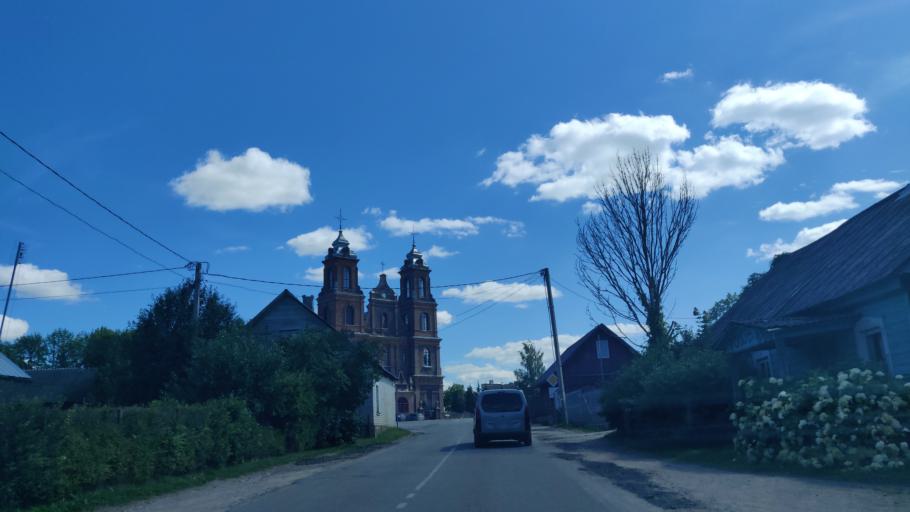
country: LT
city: Salcininkai
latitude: 54.4564
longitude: 25.5068
